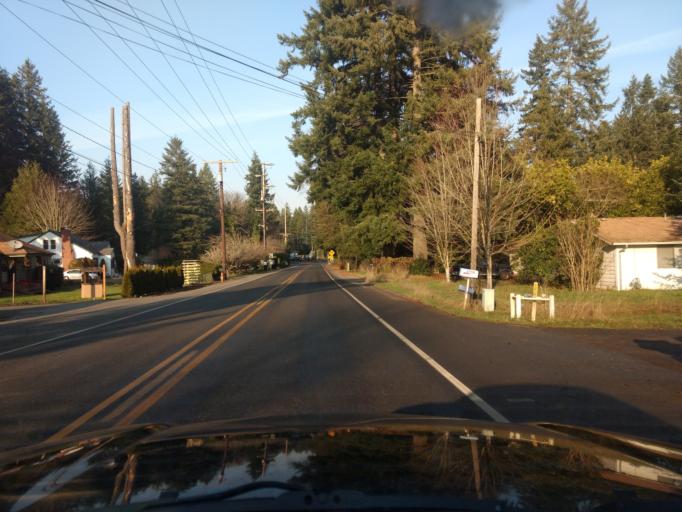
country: US
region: Washington
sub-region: Kitsap County
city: Erlands Point-Kitsap Lake
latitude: 47.5876
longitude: -122.7139
